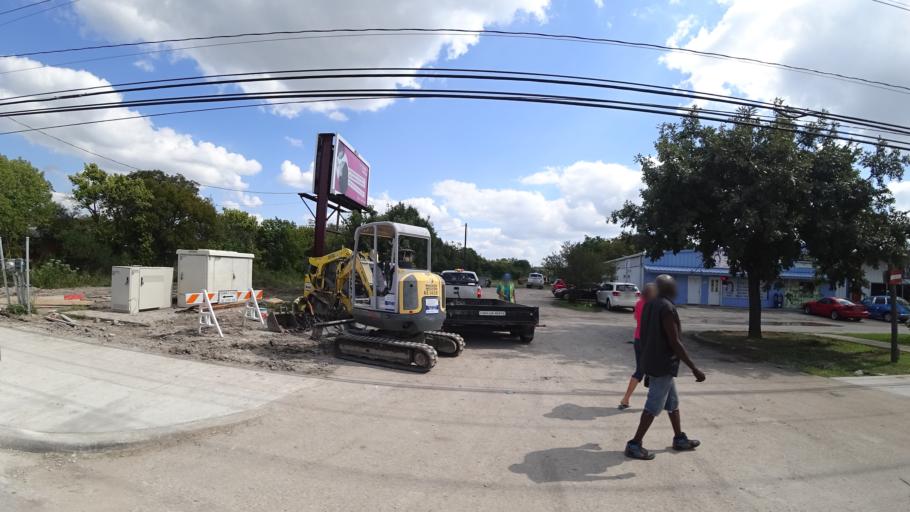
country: US
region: Texas
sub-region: Travis County
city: Wells Branch
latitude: 30.3570
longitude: -97.7006
